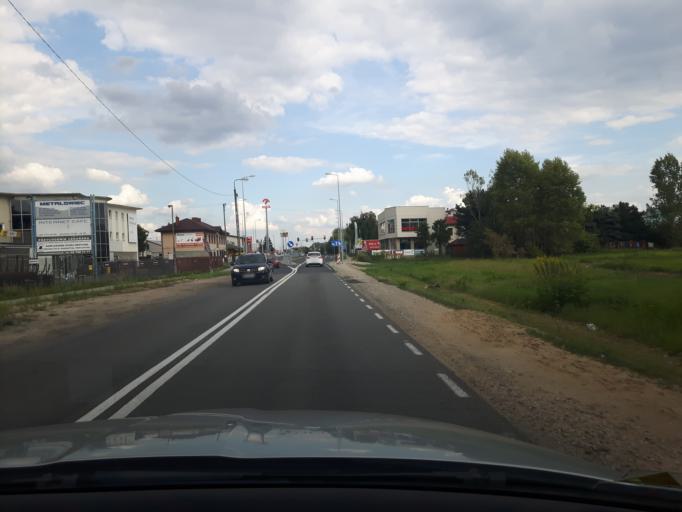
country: PL
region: Masovian Voivodeship
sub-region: Powiat piaseczynski
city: Piaseczno
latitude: 52.0819
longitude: 21.0122
